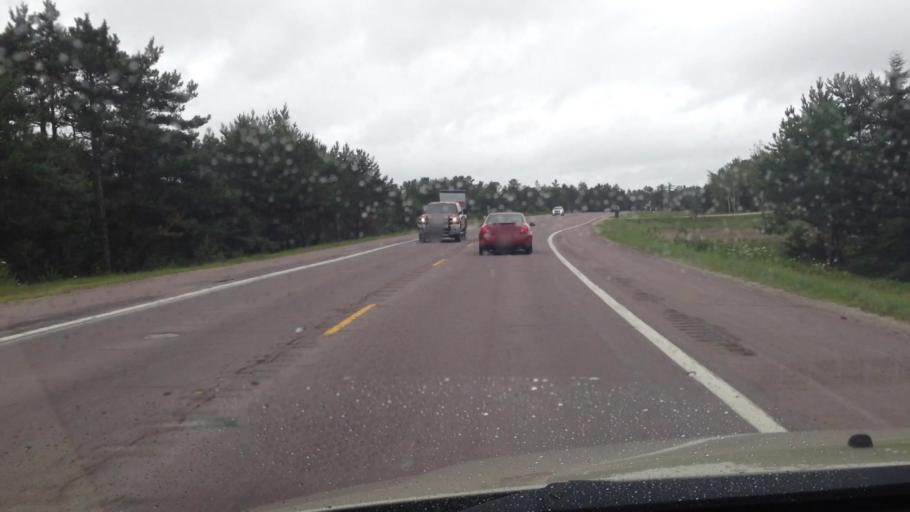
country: US
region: Michigan
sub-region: Schoolcraft County
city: Manistique
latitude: 45.9439
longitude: -86.2779
